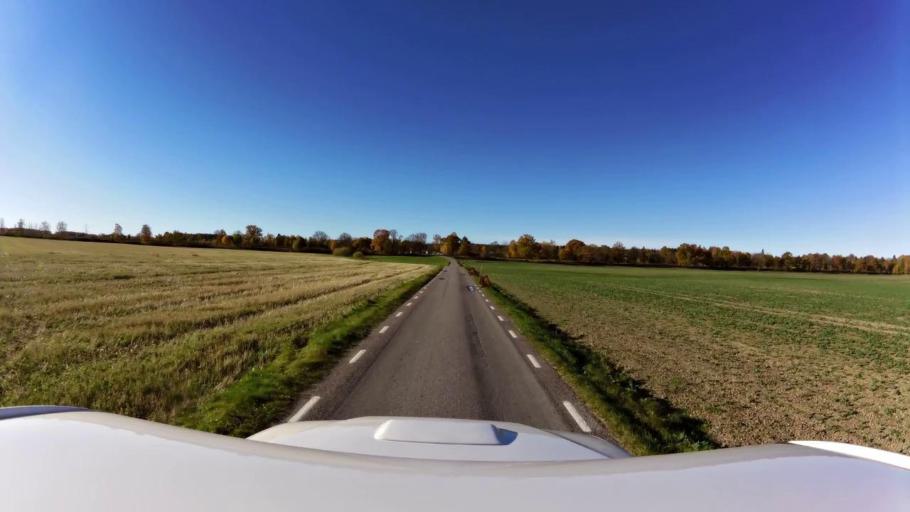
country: SE
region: OEstergoetland
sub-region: Linkopings Kommun
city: Ljungsbro
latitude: 58.5348
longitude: 15.3967
